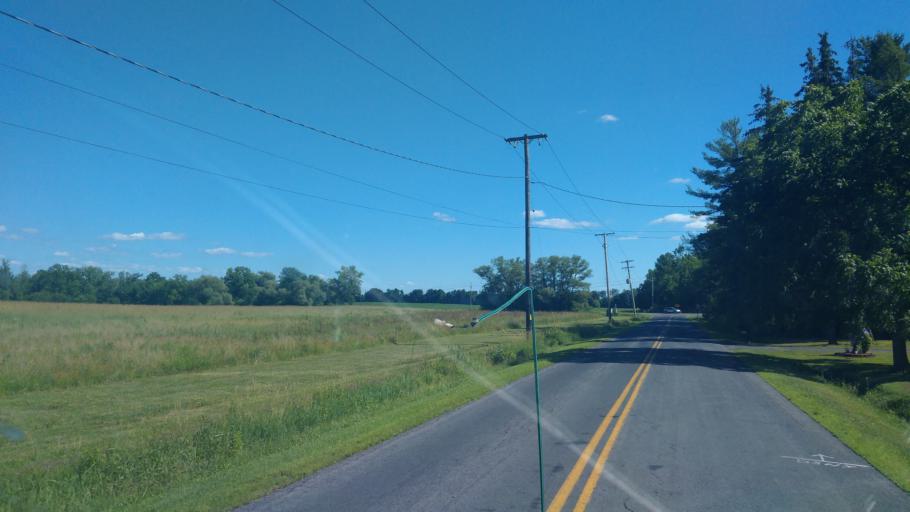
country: US
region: New York
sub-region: Seneca County
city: Seneca Falls
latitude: 42.9573
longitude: -76.8159
